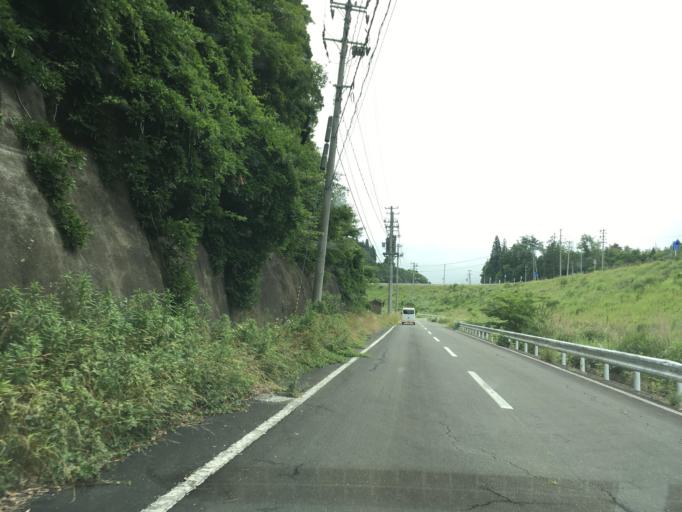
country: JP
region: Iwate
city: Ofunato
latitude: 38.9045
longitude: 141.6234
